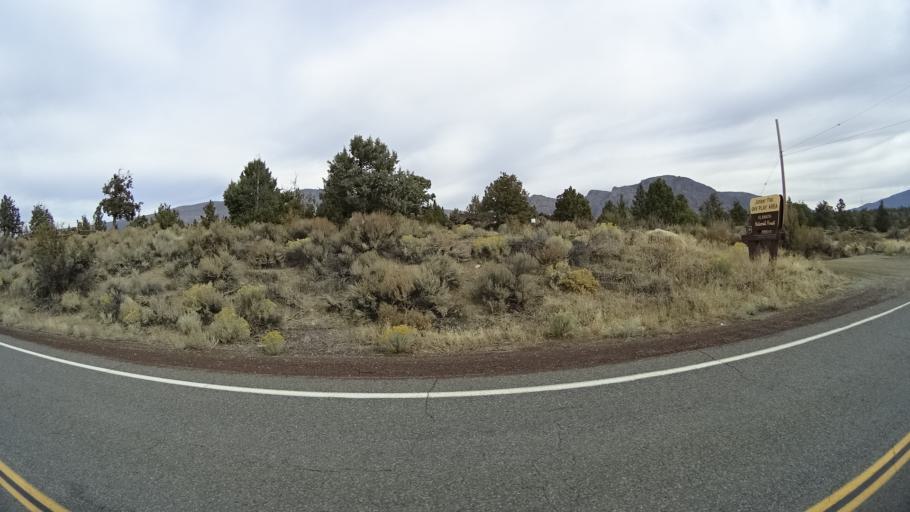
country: US
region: California
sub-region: Siskiyou County
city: Weed
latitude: 41.5684
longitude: -122.2674
